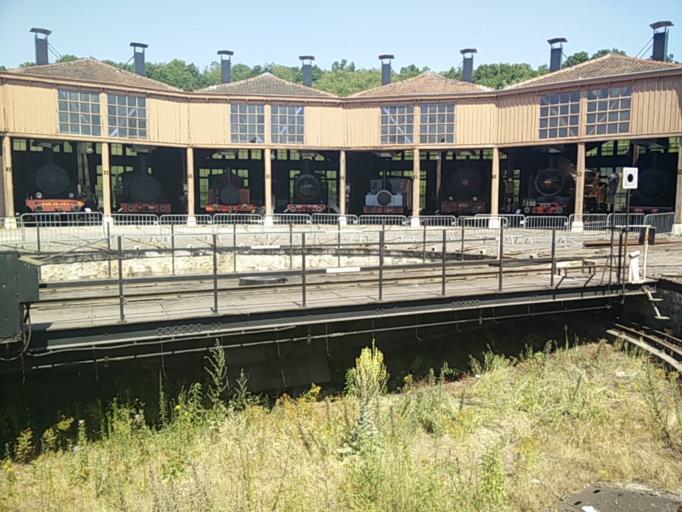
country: FR
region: Ile-de-France
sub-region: Departement de Seine-et-Marne
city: Longueville
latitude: 48.5123
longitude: 3.2555
